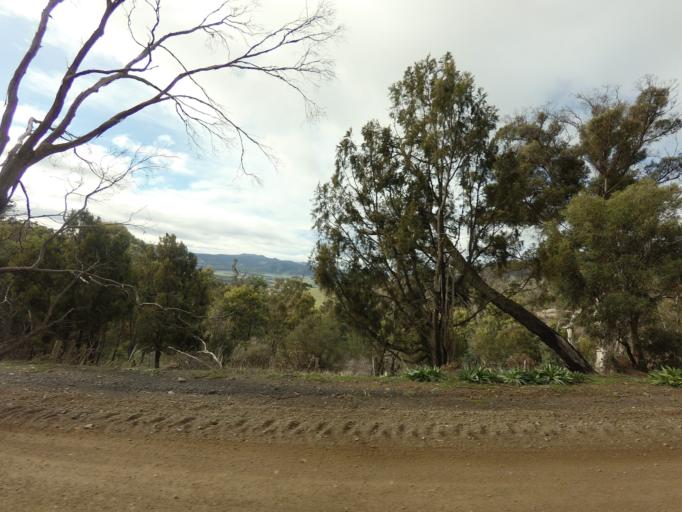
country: AU
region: Tasmania
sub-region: Derwent Valley
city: New Norfolk
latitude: -42.7269
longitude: 146.8669
